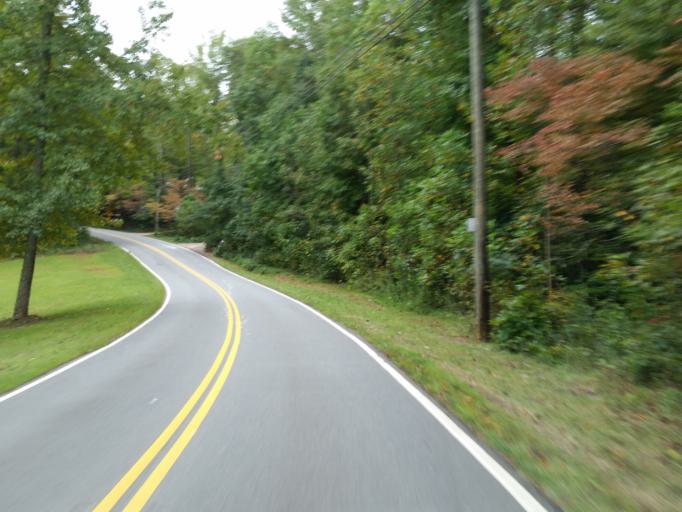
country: US
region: Georgia
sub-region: Cherokee County
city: Woodstock
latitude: 34.0770
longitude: -84.4725
